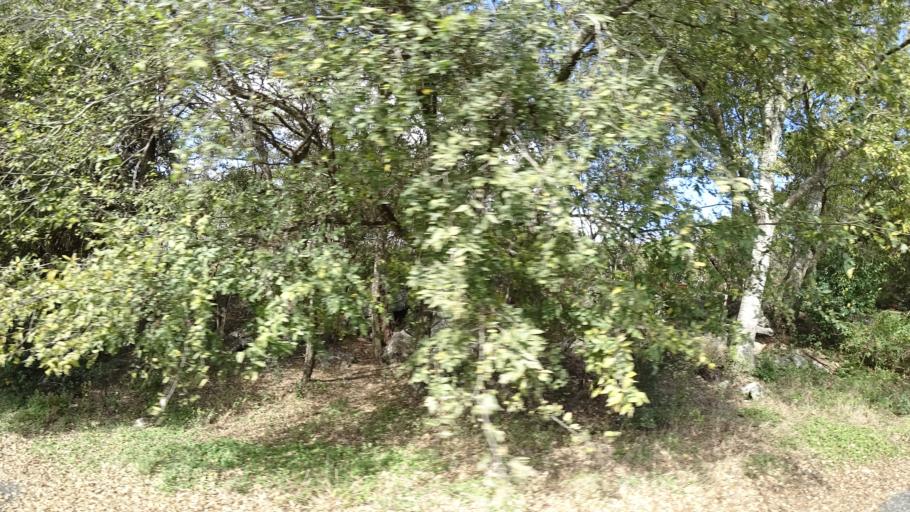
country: US
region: Texas
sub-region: Williamson County
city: Jollyville
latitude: 30.4170
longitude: -97.7855
